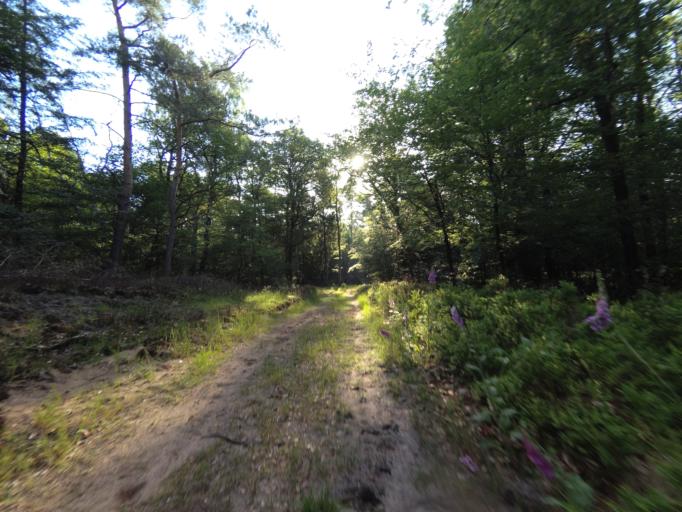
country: NL
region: Gelderland
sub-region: Gemeente Apeldoorn
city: Beekbergen
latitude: 52.1305
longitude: 5.8695
